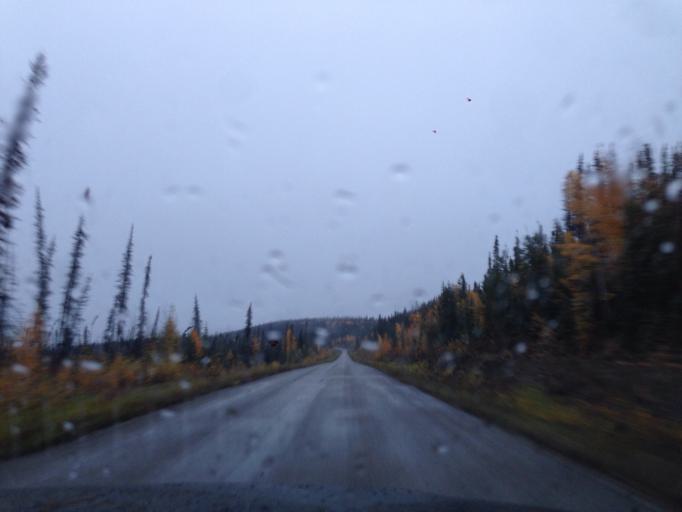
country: CA
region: Yukon
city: Watson Lake
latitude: 59.6872
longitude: -129.1511
